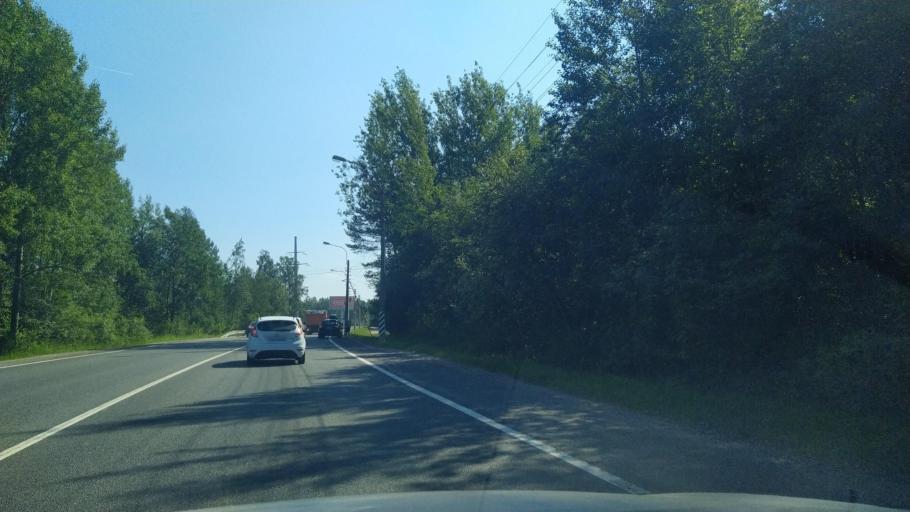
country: RU
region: St.-Petersburg
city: Beloostrov
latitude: 60.1362
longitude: 29.9886
